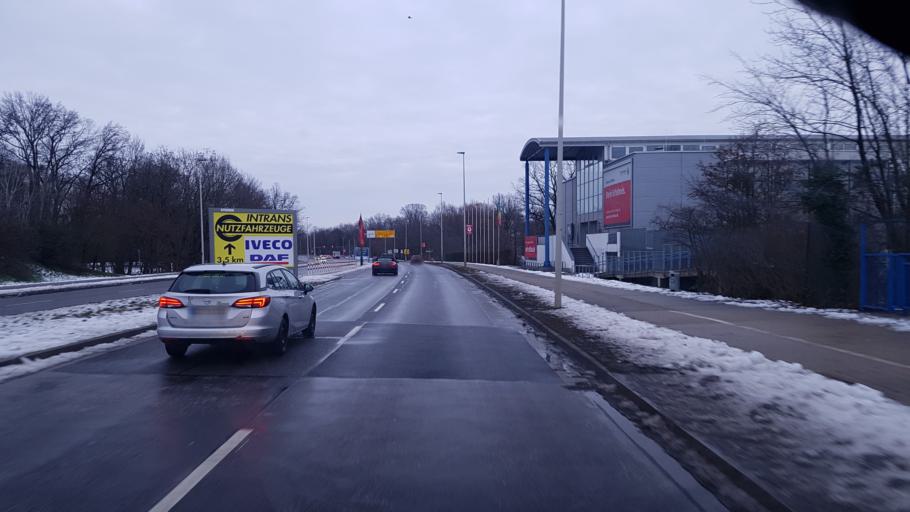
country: DE
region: Brandenburg
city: Cottbus
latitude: 51.7506
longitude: 14.3471
